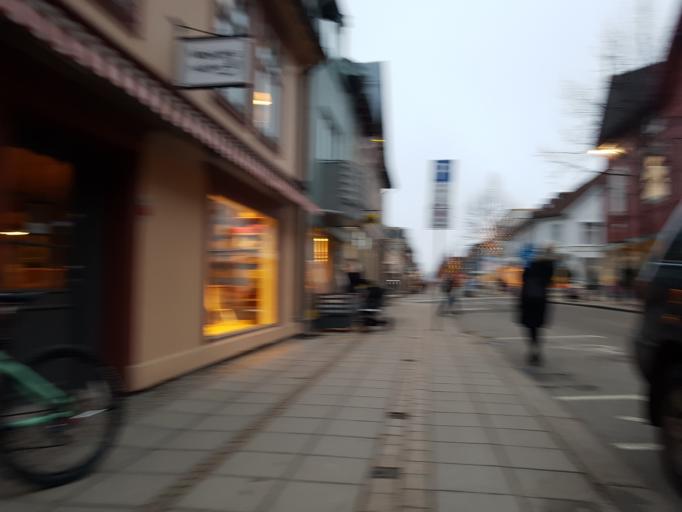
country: NO
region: Oppland
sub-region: Lillehammer
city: Lillehammer
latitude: 61.1136
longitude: 10.4674
